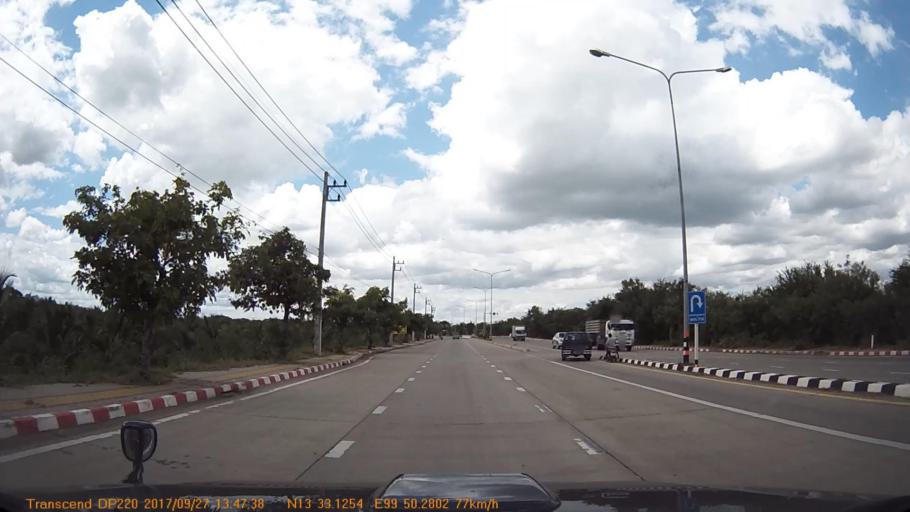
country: TH
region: Ratchaburi
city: Ratchaburi
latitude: 13.5521
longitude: 99.8380
